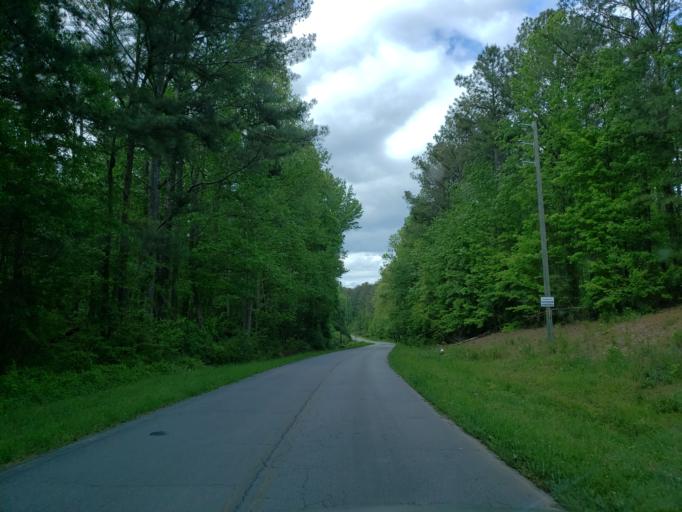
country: US
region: Georgia
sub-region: Haralson County
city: Tallapoosa
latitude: 33.7259
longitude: -85.2931
